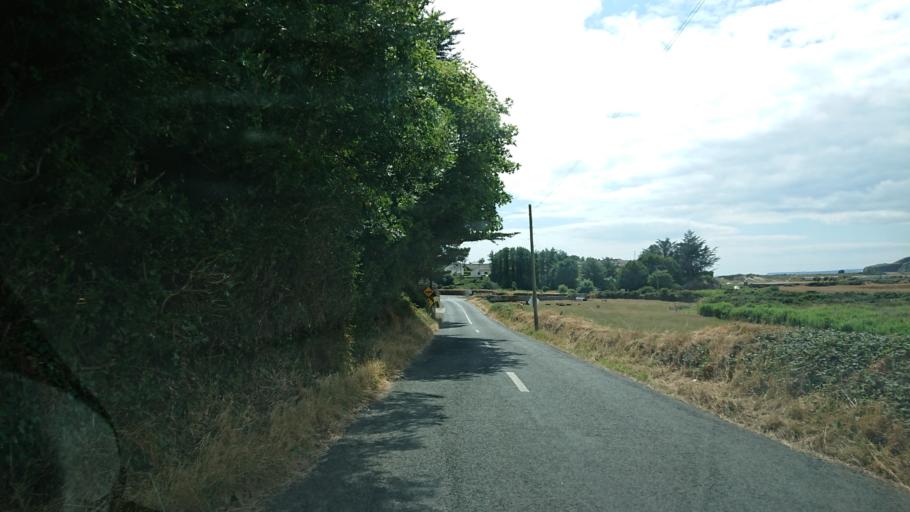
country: IE
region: Munster
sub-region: Waterford
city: Portlaw
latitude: 52.1429
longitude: -7.3572
